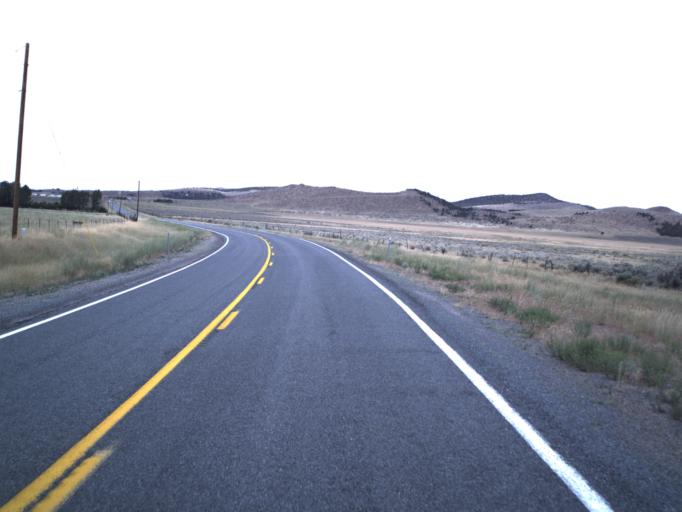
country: US
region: Utah
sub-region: Beaver County
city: Beaver
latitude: 38.6046
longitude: -112.5844
